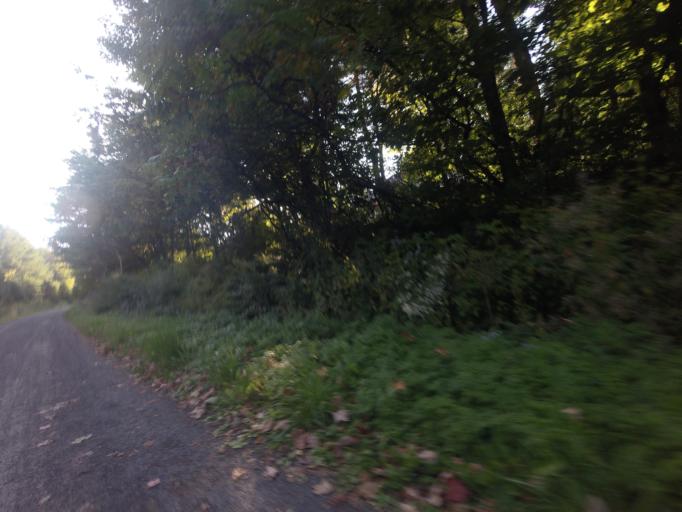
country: CA
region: Quebec
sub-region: Laurentides
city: Saint-Jerome
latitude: 45.8109
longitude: -74.0270
